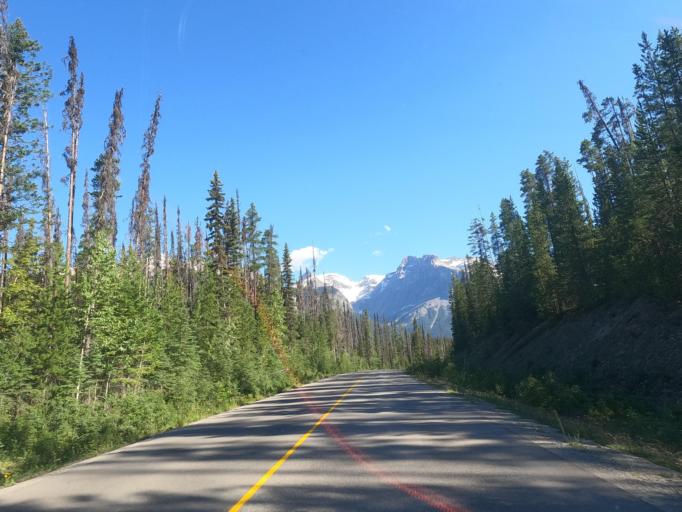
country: CA
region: Alberta
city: Lake Louise
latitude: 51.4179
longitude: -116.5337
